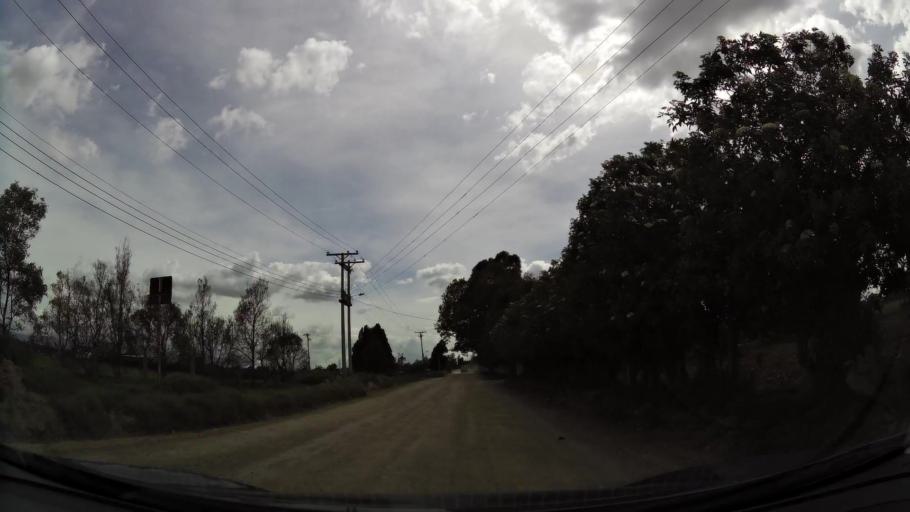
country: CO
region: Cundinamarca
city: Funza
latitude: 4.7177
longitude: -74.1700
